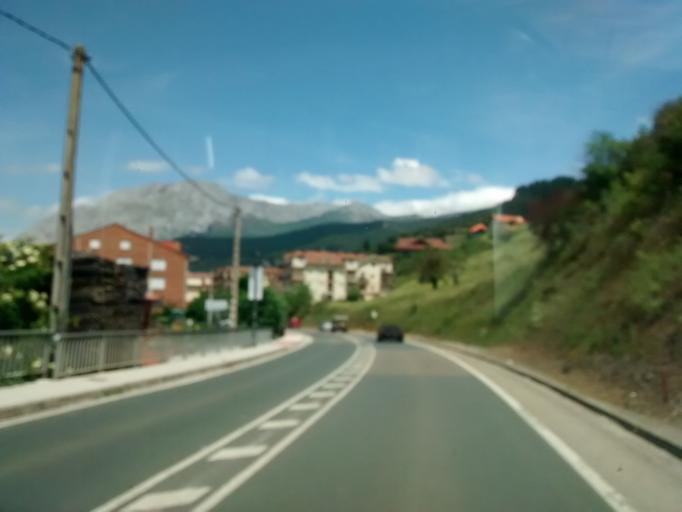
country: ES
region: Cantabria
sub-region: Provincia de Cantabria
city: Potes
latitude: 43.1580
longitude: -4.6148
